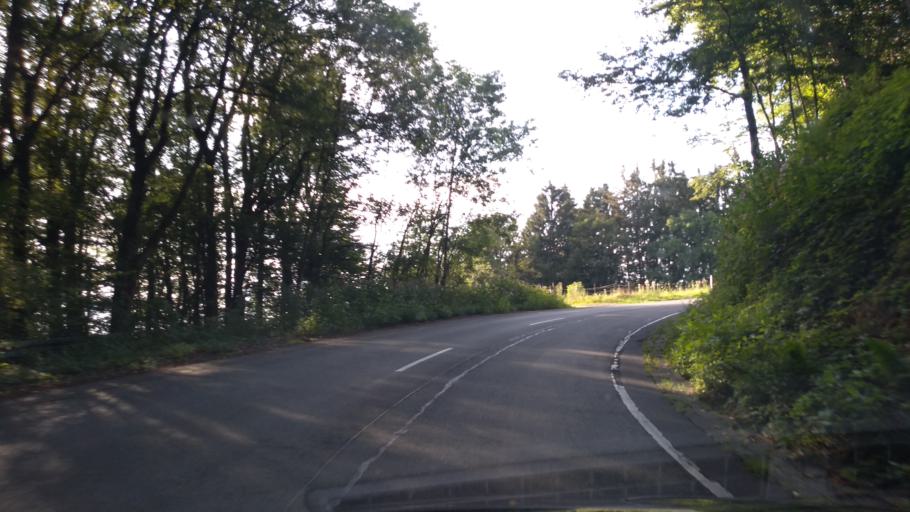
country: DE
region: North Rhine-Westphalia
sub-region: Regierungsbezirk Koln
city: Engelskirchen
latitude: 50.9771
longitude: 7.4438
